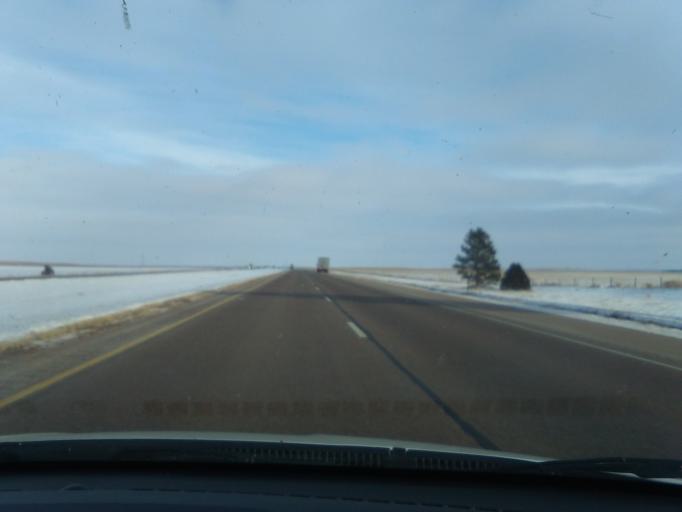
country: US
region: Nebraska
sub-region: Cheyenne County
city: Sidney
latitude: 41.1134
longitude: -102.8590
